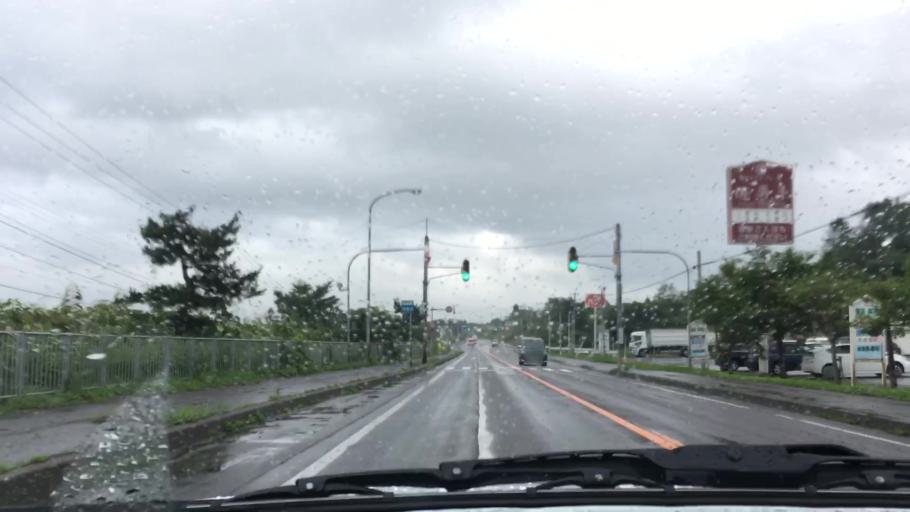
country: JP
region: Hokkaido
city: Nanae
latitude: 42.2360
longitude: 140.3100
